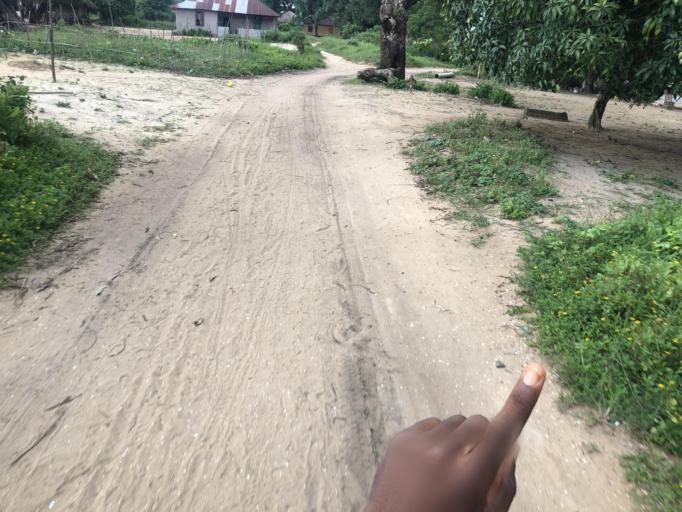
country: SL
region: Southern Province
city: Bonthe
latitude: 7.5234
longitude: -12.5078
